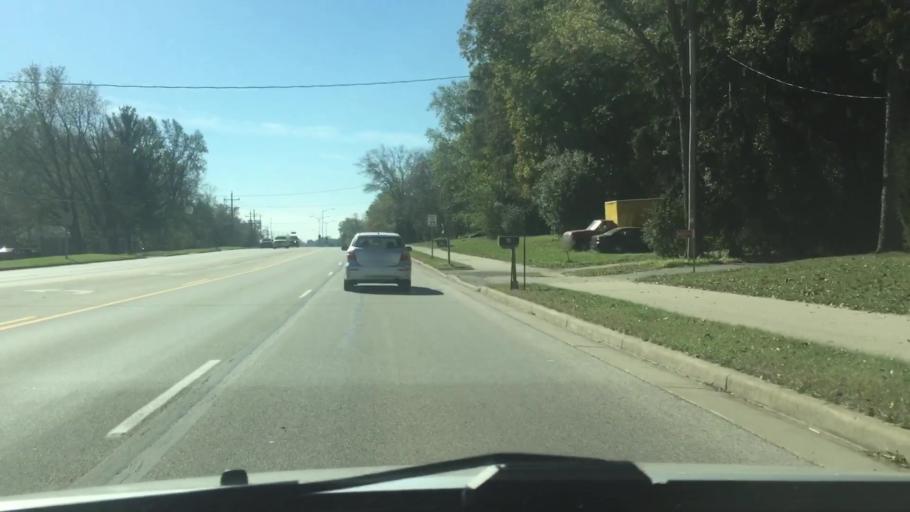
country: US
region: Wisconsin
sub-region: Waukesha County
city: Waukesha
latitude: 42.9956
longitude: -88.2609
